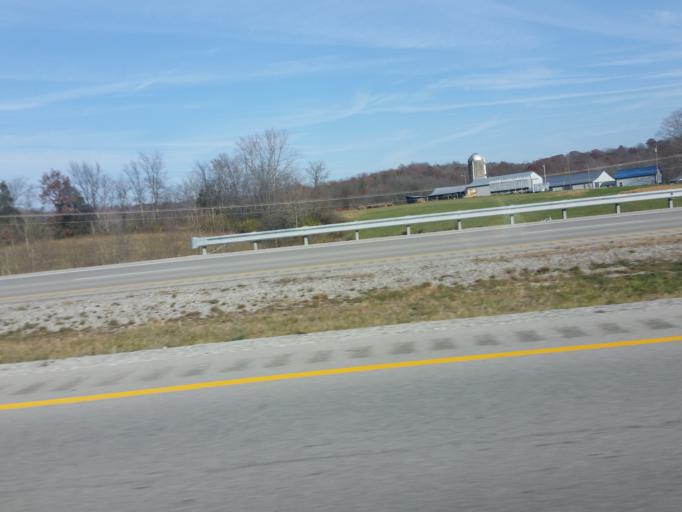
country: US
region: Kentucky
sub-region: Campbell County
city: Claryville
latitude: 38.8550
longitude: -84.3848
